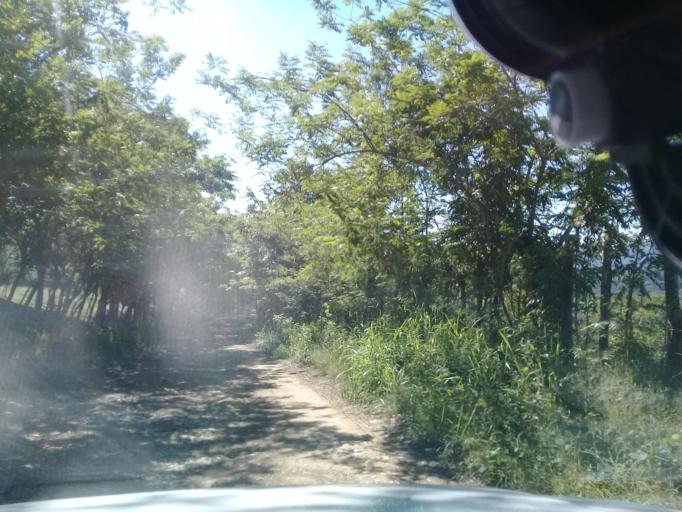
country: MX
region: Hidalgo
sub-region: Huejutla de Reyes
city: Huejutla de Reyes
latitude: 21.1641
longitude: -98.4133
